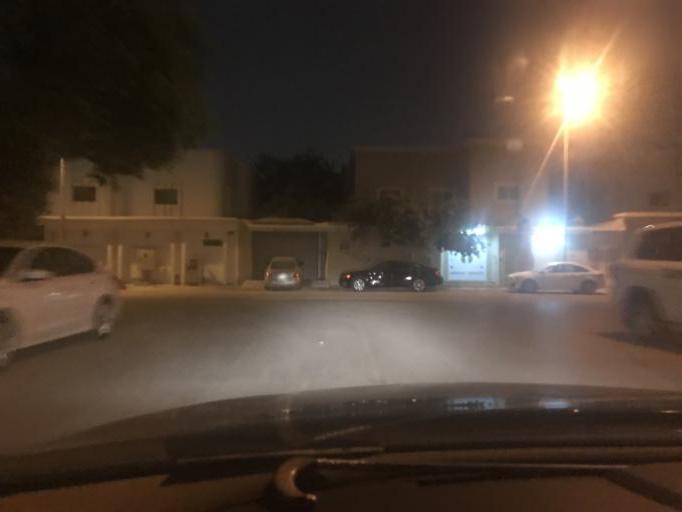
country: SA
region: Ar Riyad
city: Riyadh
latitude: 24.7605
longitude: 46.7620
